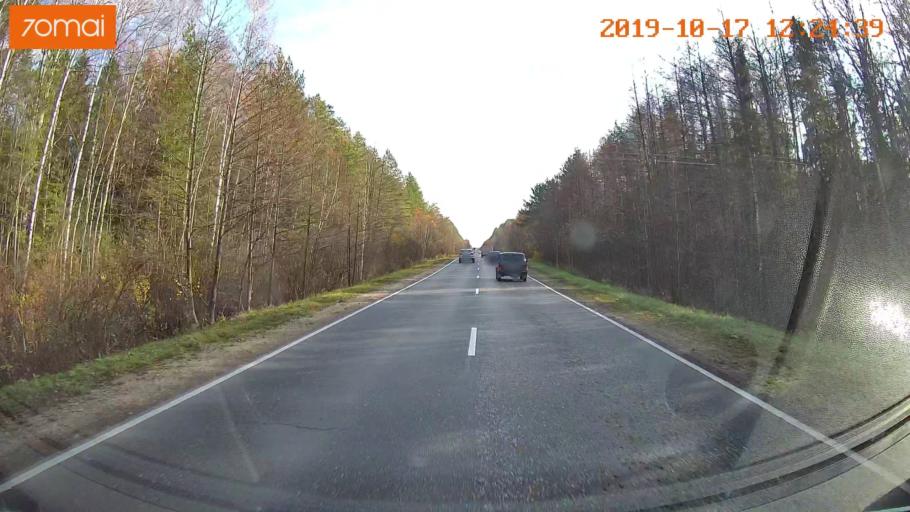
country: RU
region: Rjazan
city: Gus'-Zheleznyy
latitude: 55.0337
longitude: 41.2195
